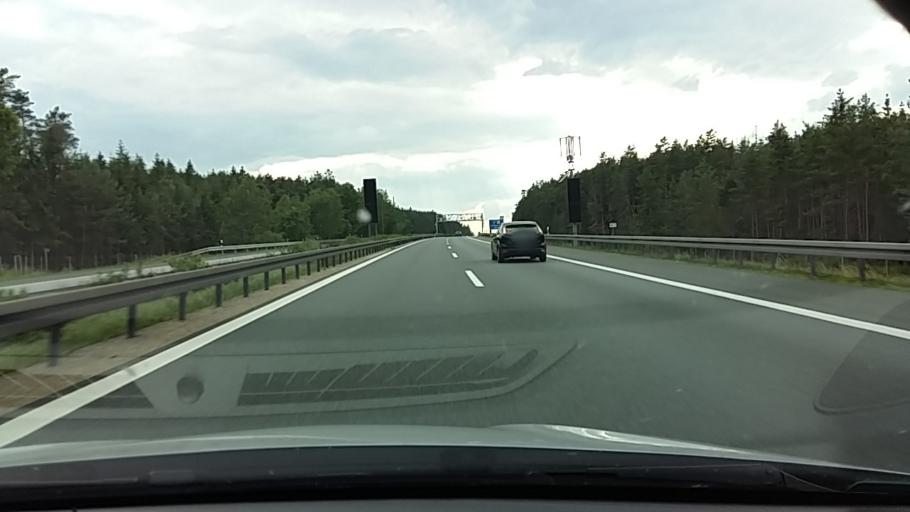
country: DE
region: Bavaria
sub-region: Upper Palatinate
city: Kummersbruck
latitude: 49.3937
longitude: 11.8736
